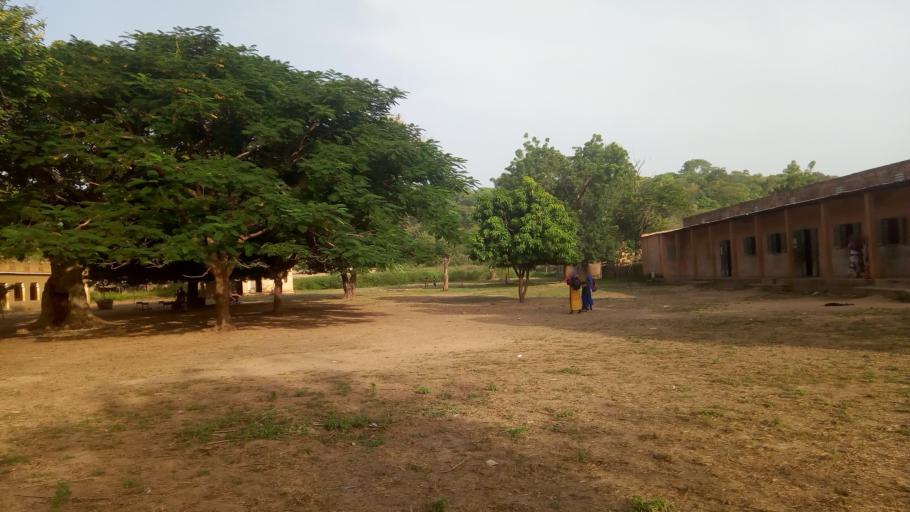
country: ML
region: Kayes
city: Kita
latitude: 13.1298
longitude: -8.8302
